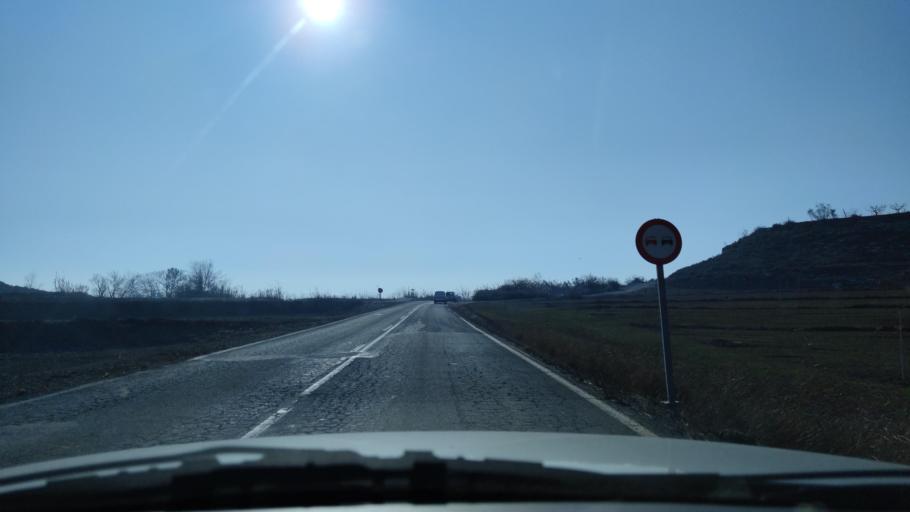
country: ES
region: Catalonia
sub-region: Provincia de Lleida
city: Juneda
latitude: 41.5644
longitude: 0.7480
